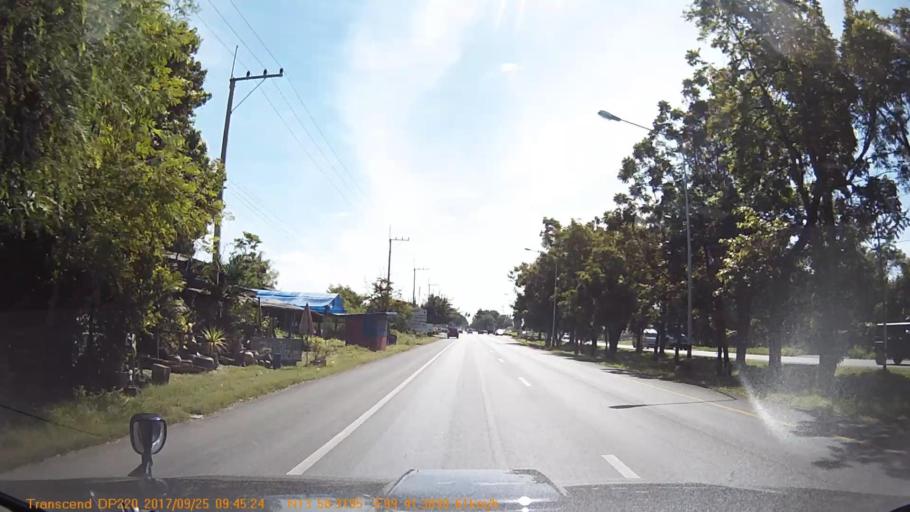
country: TH
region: Kanchanaburi
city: Tha Muang
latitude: 13.9719
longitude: 99.6901
